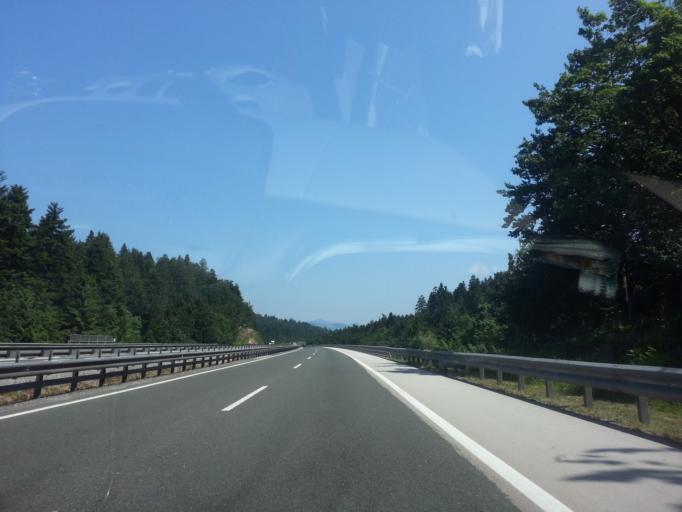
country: SI
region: Logatec
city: Logatec
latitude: 45.9256
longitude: 14.2694
